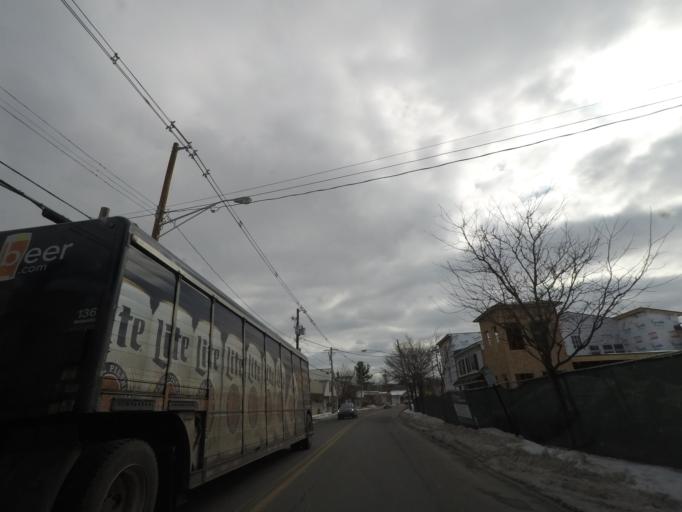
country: US
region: New York
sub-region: Washington County
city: Greenwich
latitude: 43.0894
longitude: -73.4983
